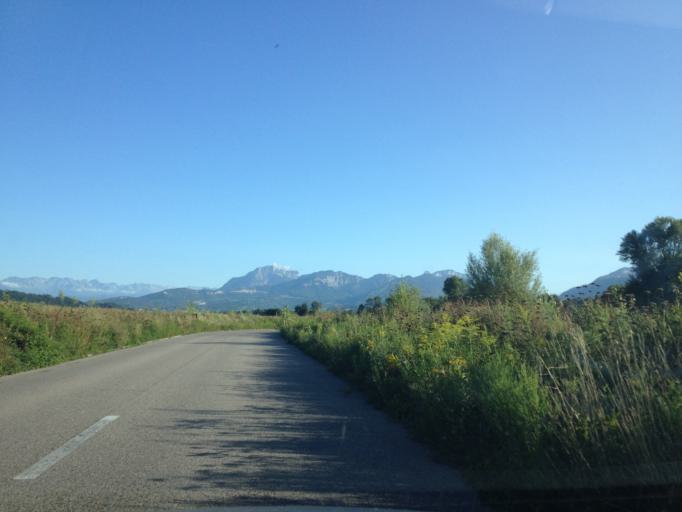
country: FR
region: Rhone-Alpes
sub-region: Departement de la Savoie
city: Le Bourget-du-Lac
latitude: 45.6392
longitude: 5.8751
